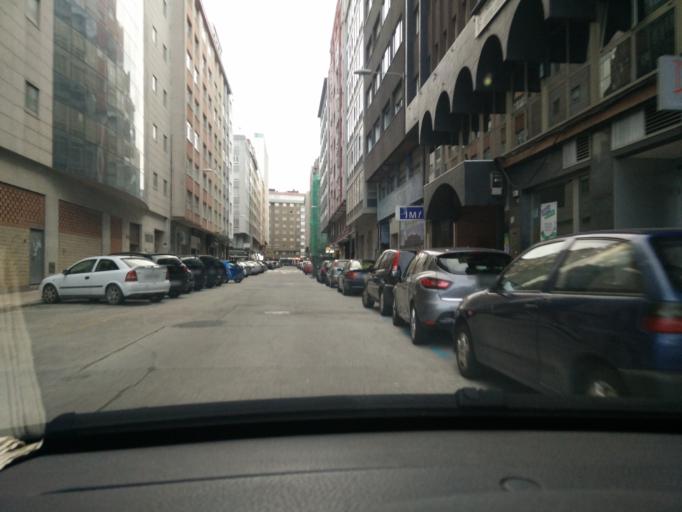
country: ES
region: Galicia
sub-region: Provincia da Coruna
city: A Coruna
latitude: 43.3571
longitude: -8.3993
